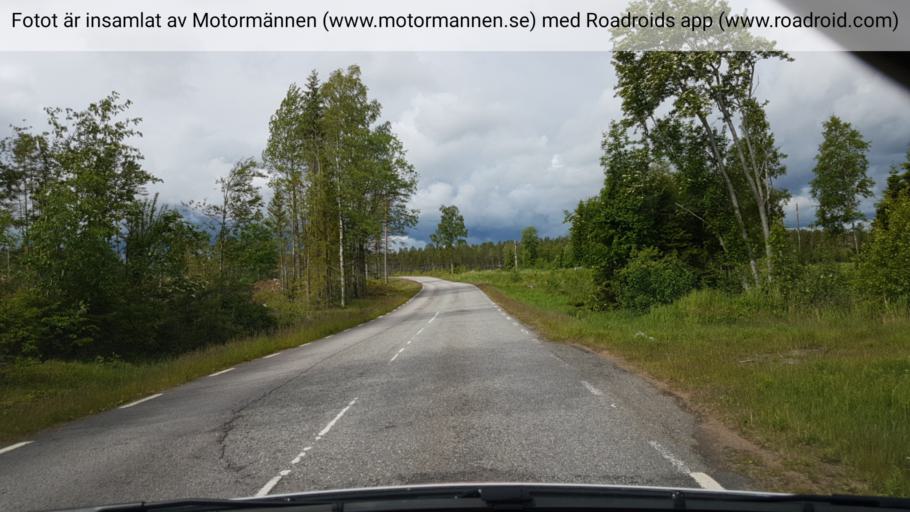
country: SE
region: Vaesterbotten
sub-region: Umea Kommun
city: Hoernefors
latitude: 63.5630
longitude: 19.7594
